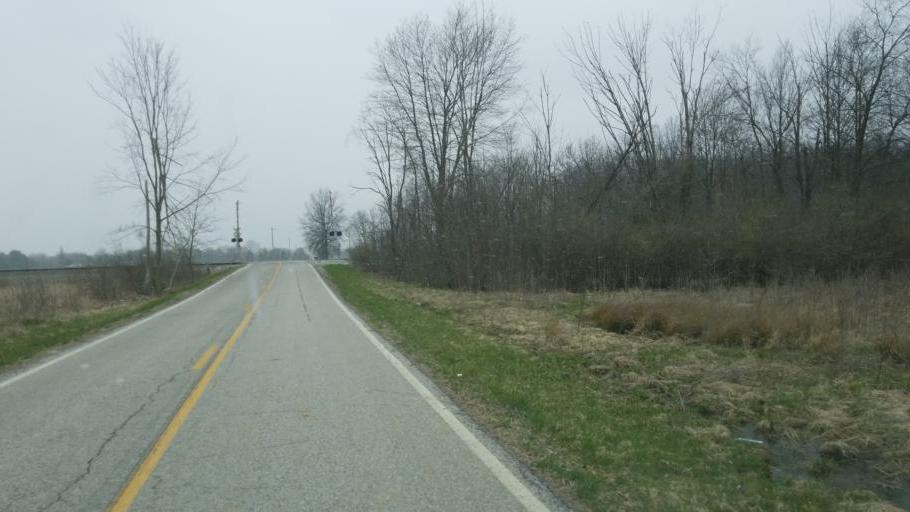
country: US
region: Ohio
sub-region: Delaware County
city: Delaware
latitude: 40.3797
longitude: -83.0808
